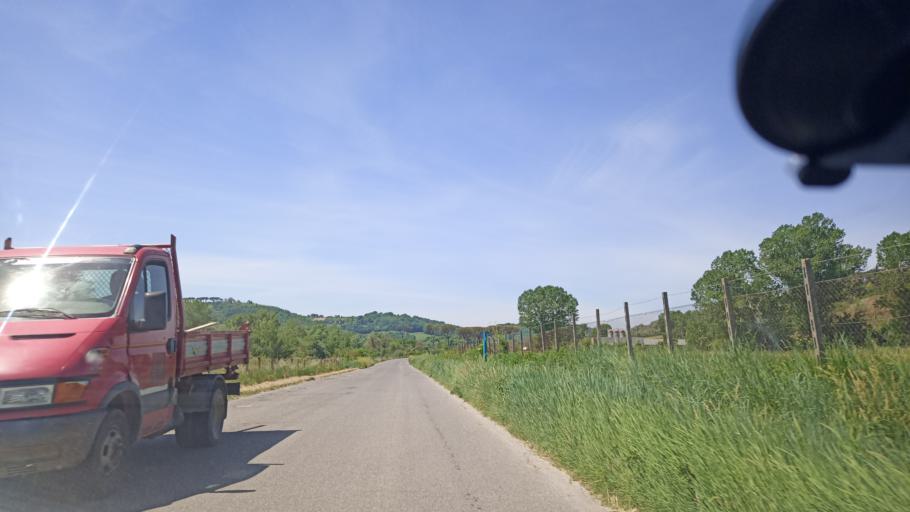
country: IT
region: Latium
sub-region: Provincia di Rieti
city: Stimigliano
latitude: 42.3173
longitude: 12.5799
